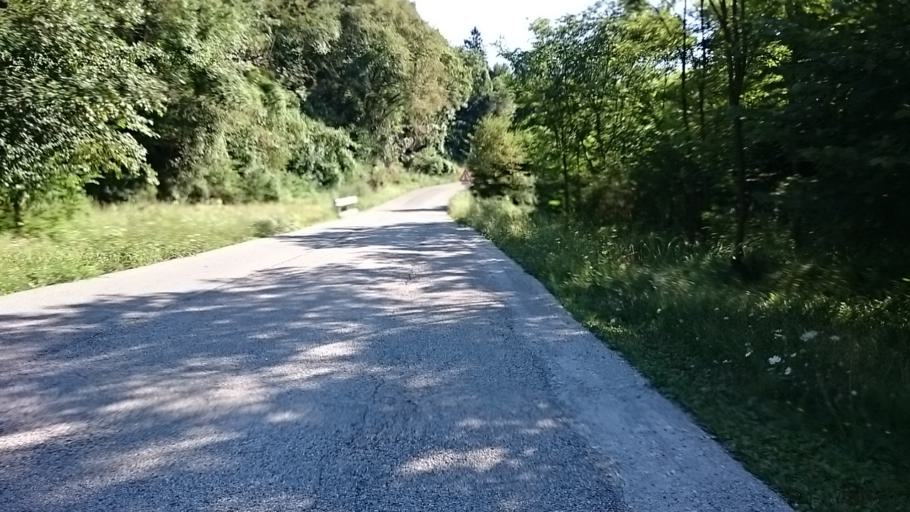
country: IT
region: Veneto
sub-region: Provincia di Belluno
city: Longarone
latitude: 46.2355
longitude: 12.3065
